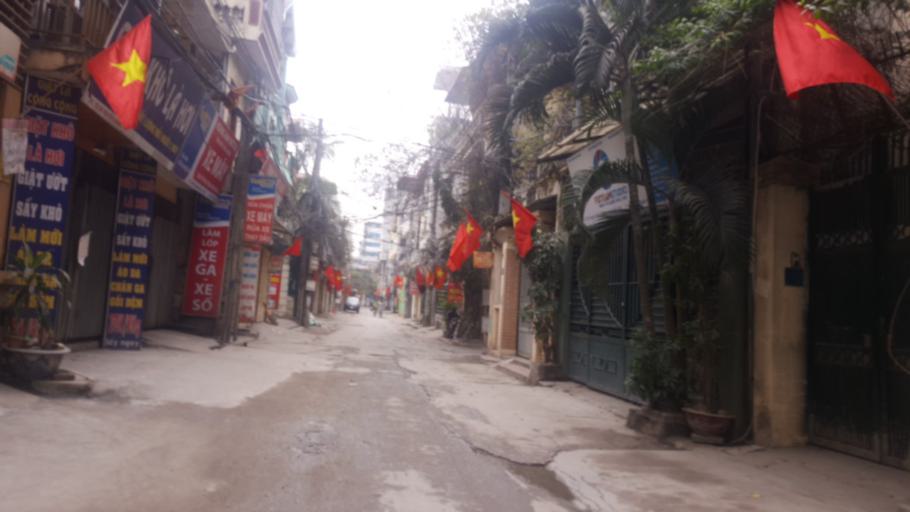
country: VN
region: Ha Noi
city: Cau Giay
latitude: 21.0281
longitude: 105.7956
